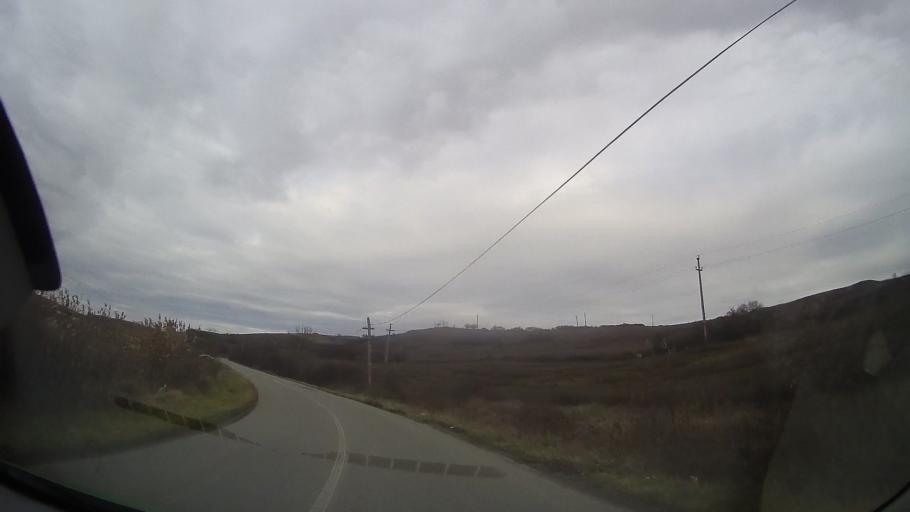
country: RO
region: Mures
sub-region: Comuna Faragau
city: Faragau
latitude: 46.7485
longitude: 24.5287
